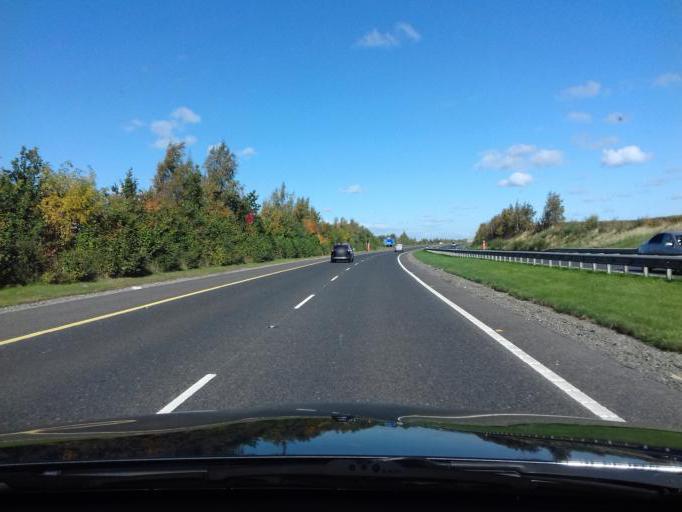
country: IE
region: Leinster
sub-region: Fingal County
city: Blanchardstown
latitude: 53.4425
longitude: -6.3557
